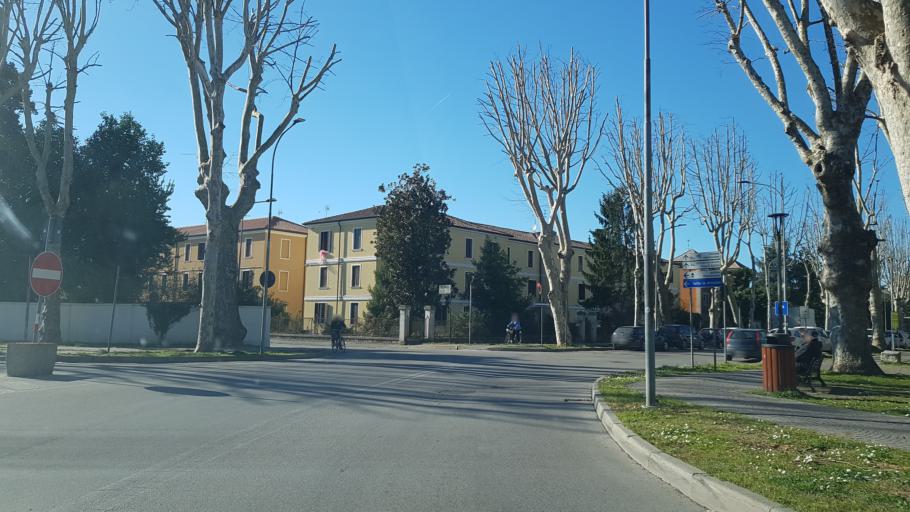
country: IT
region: Veneto
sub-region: Provincia di Rovigo
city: Adria
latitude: 45.0578
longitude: 12.0556
